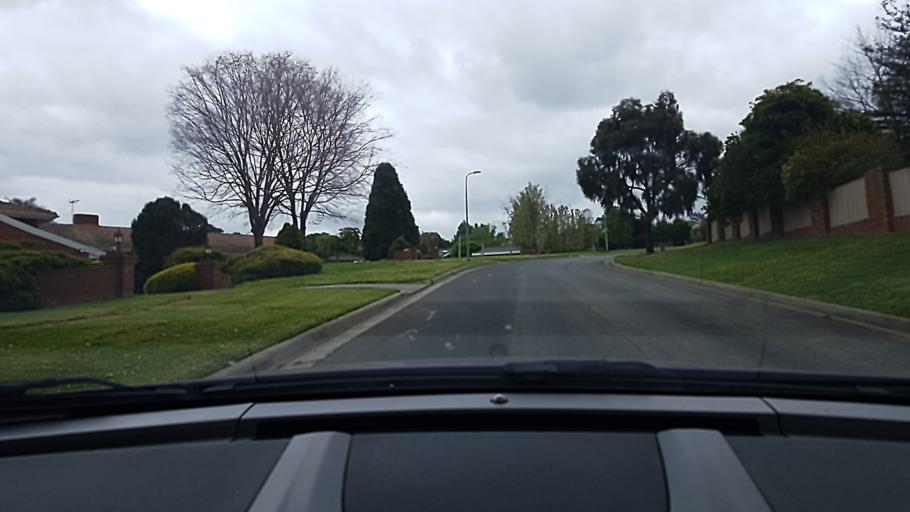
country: AU
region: Victoria
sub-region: Nillumbik
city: Eltham
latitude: -37.7503
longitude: 145.1393
